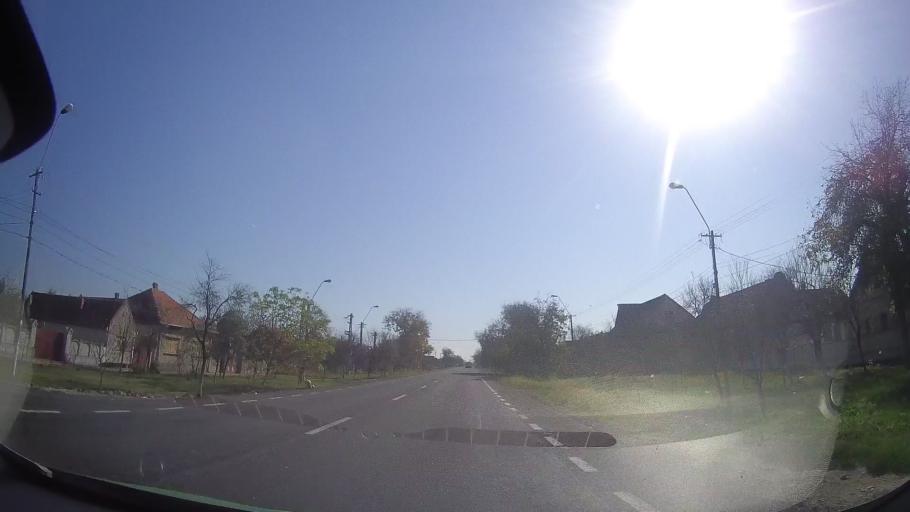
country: RO
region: Timis
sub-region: Comuna Belint
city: Belint
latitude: 45.7534
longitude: 21.7581
